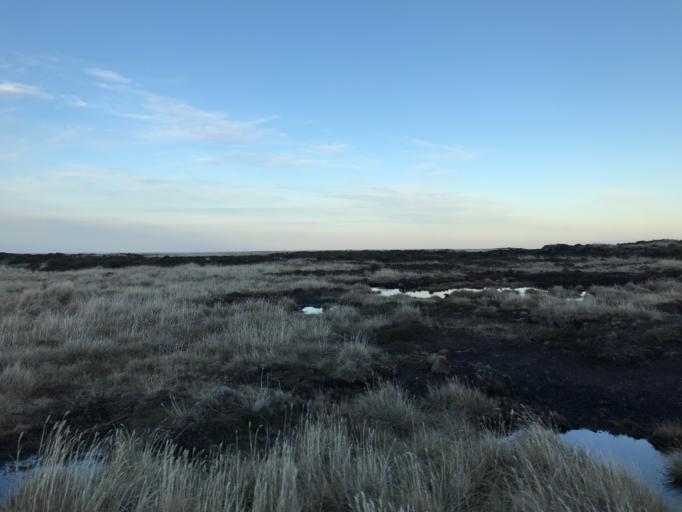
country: FK
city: Stanley
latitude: -51.7032
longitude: -57.8435
